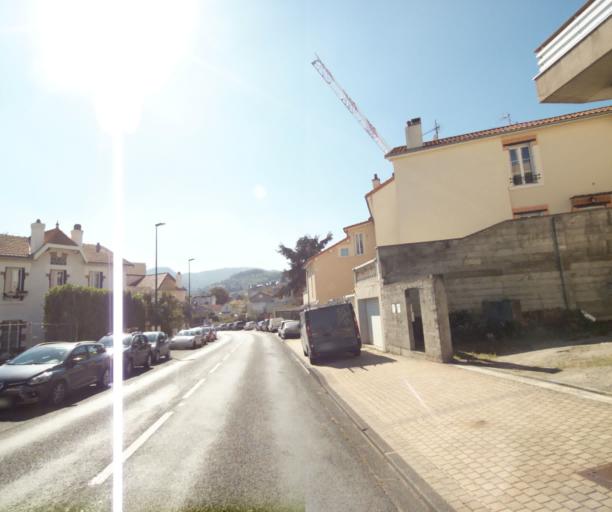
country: FR
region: Auvergne
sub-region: Departement du Puy-de-Dome
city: Chamalieres
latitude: 45.7802
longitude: 3.0627
